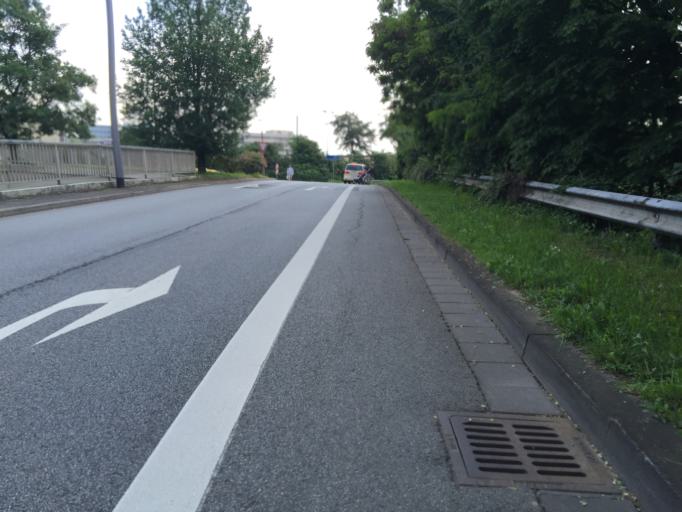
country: DE
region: Hesse
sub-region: Regierungsbezirk Darmstadt
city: Wiesbaden
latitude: 50.0741
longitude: 8.2584
